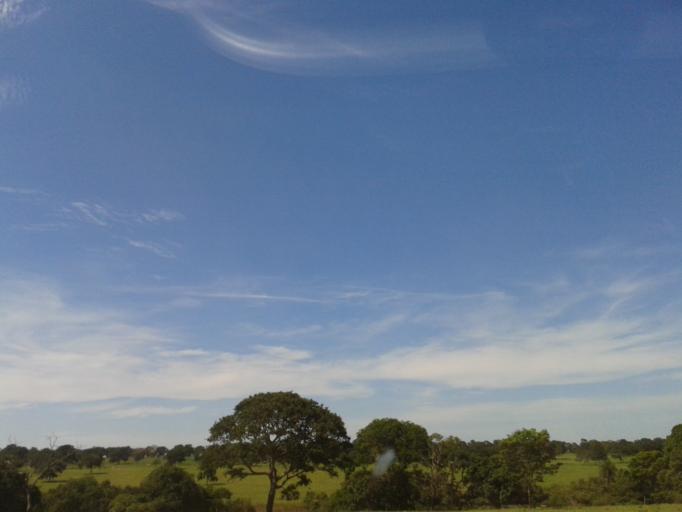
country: BR
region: Minas Gerais
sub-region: Santa Vitoria
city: Santa Vitoria
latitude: -19.1675
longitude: -50.5217
